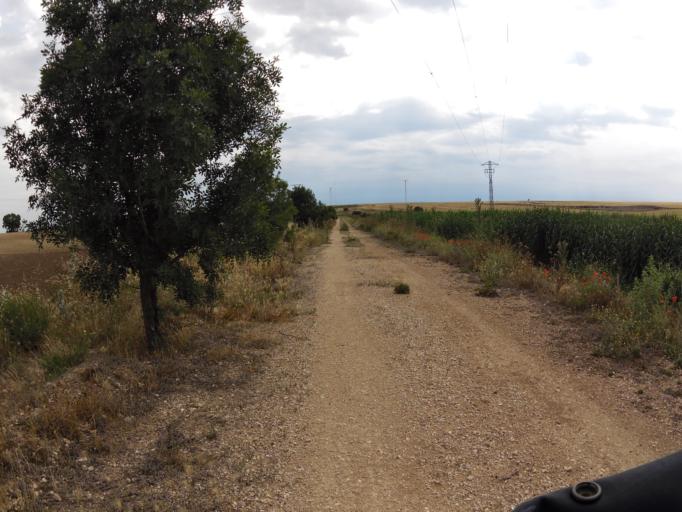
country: ES
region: Castille-La Mancha
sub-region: Provincia de Albacete
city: Albacete
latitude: 39.0412
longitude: -1.7667
